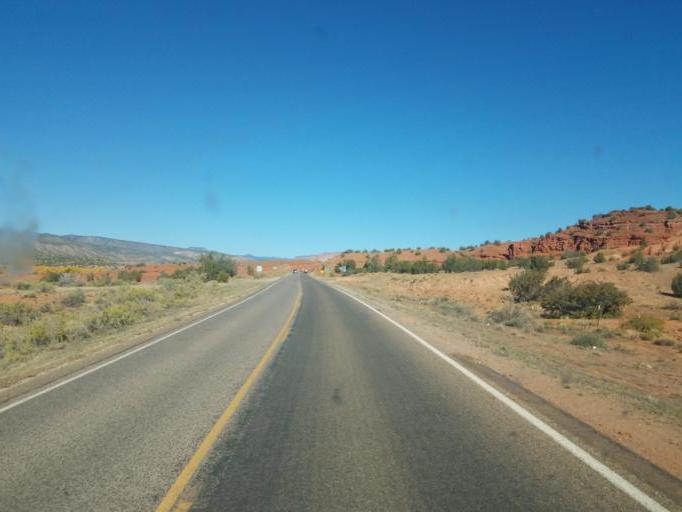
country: US
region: New Mexico
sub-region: Sandoval County
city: Jemez Pueblo
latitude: 35.6368
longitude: -106.7233
